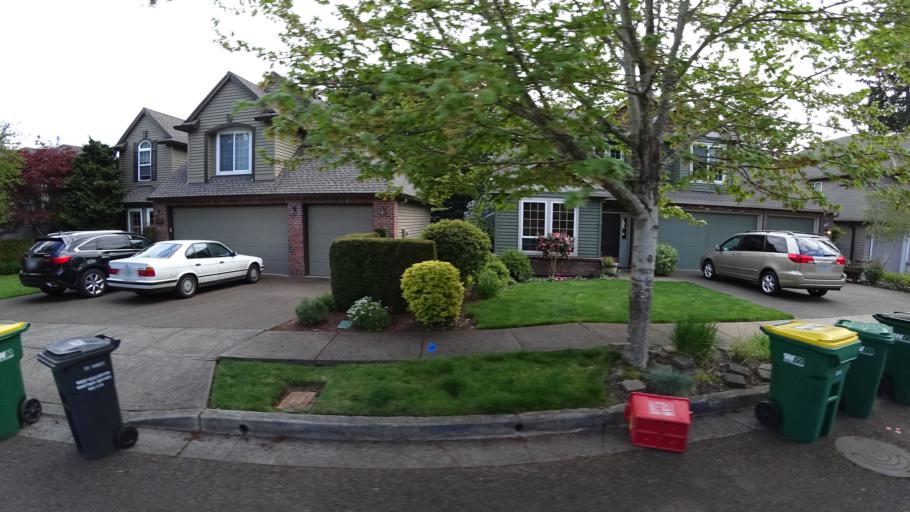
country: US
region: Oregon
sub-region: Washington County
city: Beaverton
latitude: 45.4488
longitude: -122.8323
